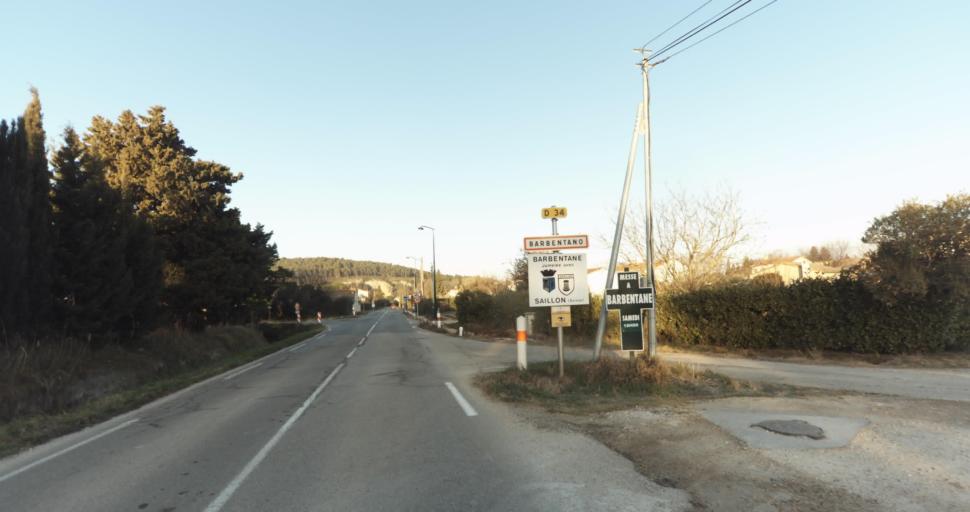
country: FR
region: Provence-Alpes-Cote d'Azur
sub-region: Departement des Bouches-du-Rhone
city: Barbentane
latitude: 43.8980
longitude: 4.7703
